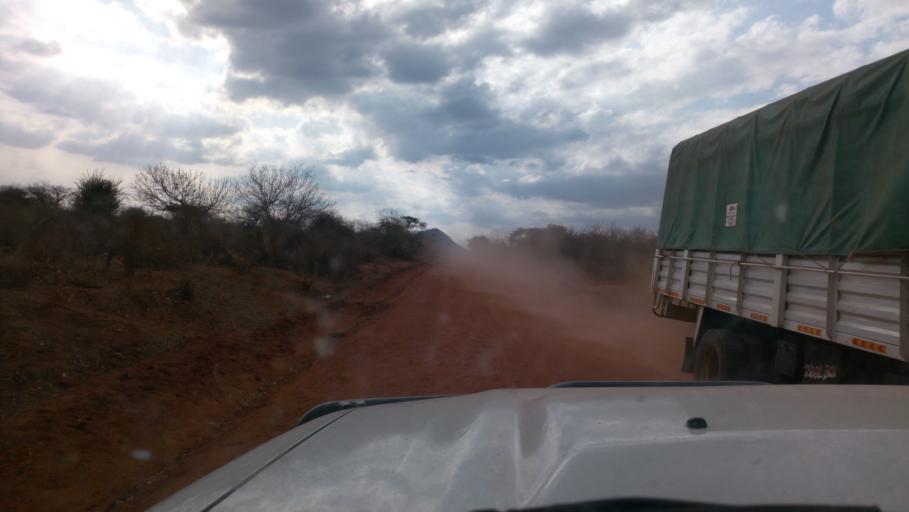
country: KE
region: Kitui
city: Kitui
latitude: -1.7248
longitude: 38.3876
